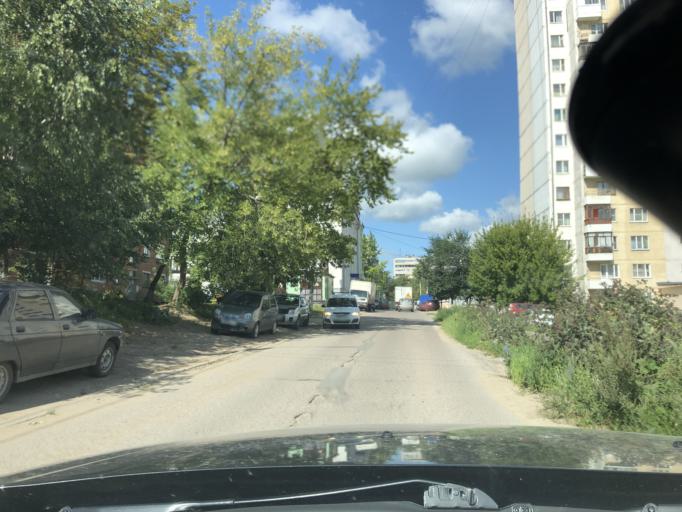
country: RU
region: Tula
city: Tula
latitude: 54.2162
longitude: 37.6259
